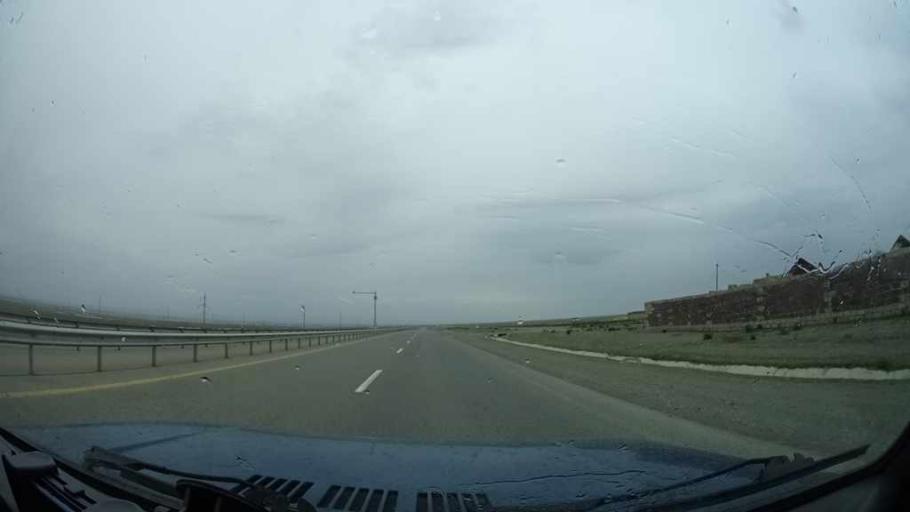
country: AZ
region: Ganja City
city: Ganja
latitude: 40.6396
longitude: 46.4167
